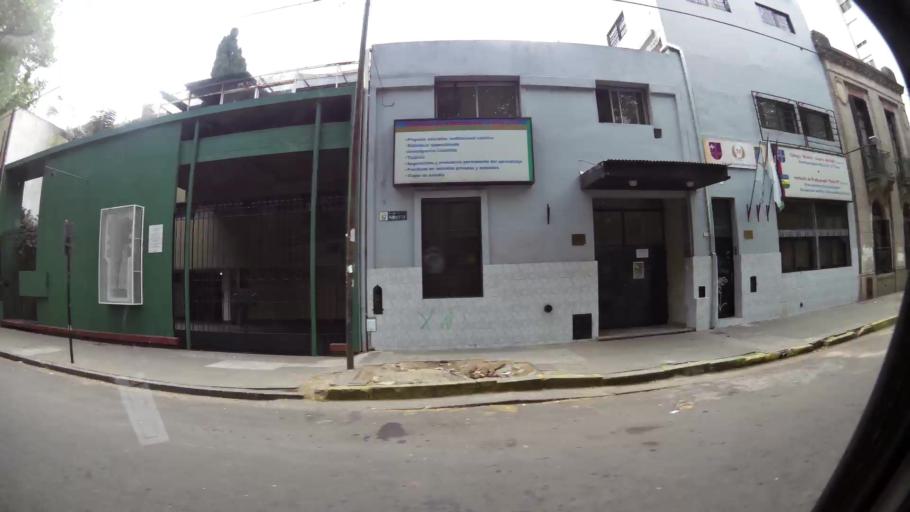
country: AR
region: Buenos Aires
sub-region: Partido de La Plata
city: La Plata
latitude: -34.9133
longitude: -57.9389
